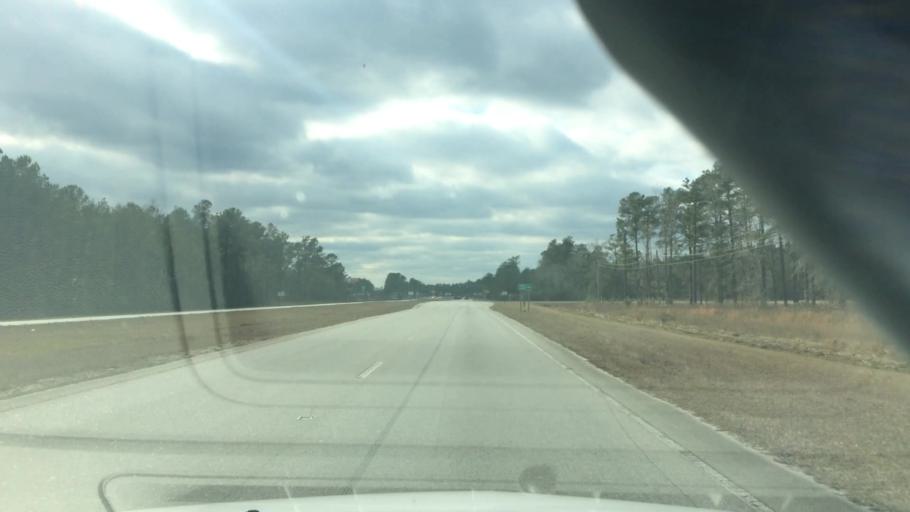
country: US
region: North Carolina
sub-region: Brunswick County
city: Bolivia
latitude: 34.0411
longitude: -78.2425
